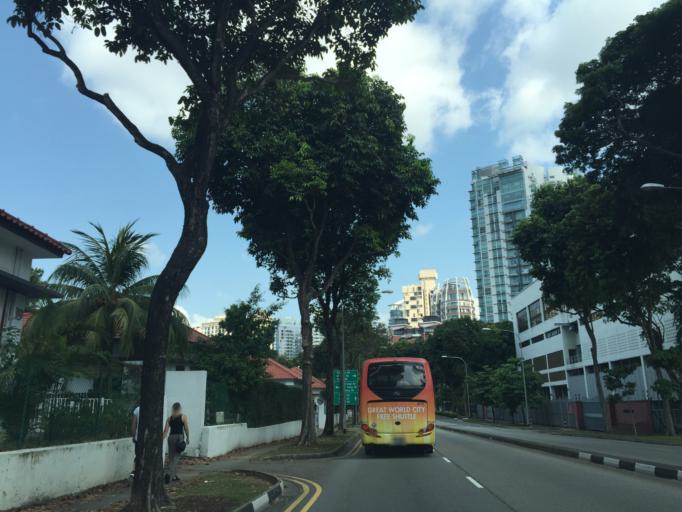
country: SG
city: Singapore
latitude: 1.2998
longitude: 103.8320
